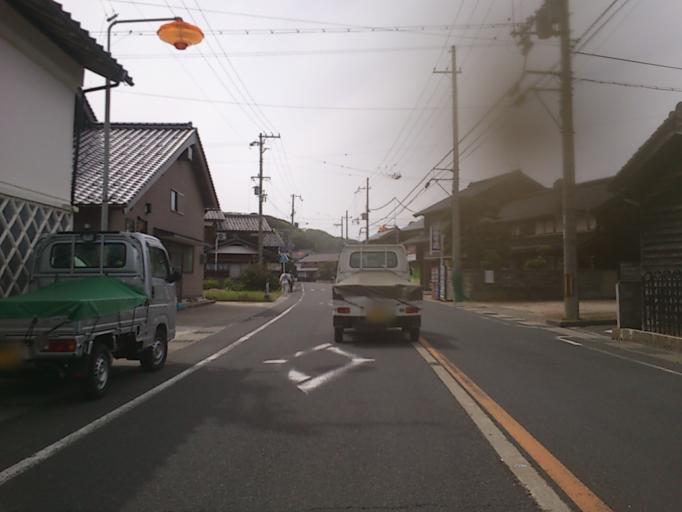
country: JP
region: Kyoto
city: Miyazu
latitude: 35.6885
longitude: 135.0201
